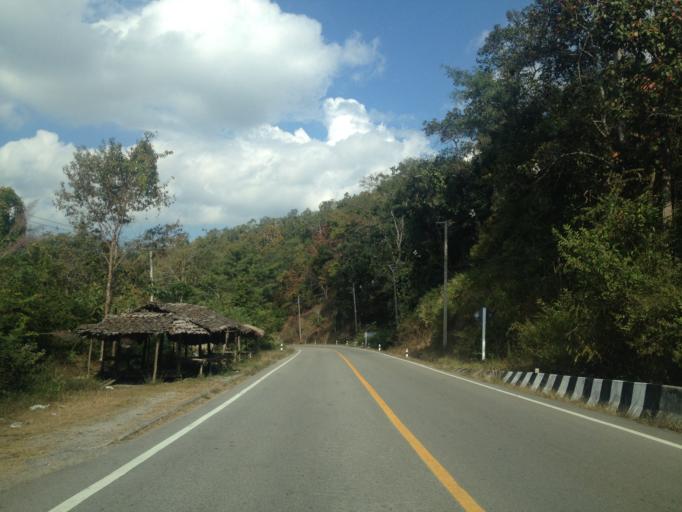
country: TH
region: Mae Hong Son
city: Ban Huai I Huak
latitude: 18.1416
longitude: 98.1703
